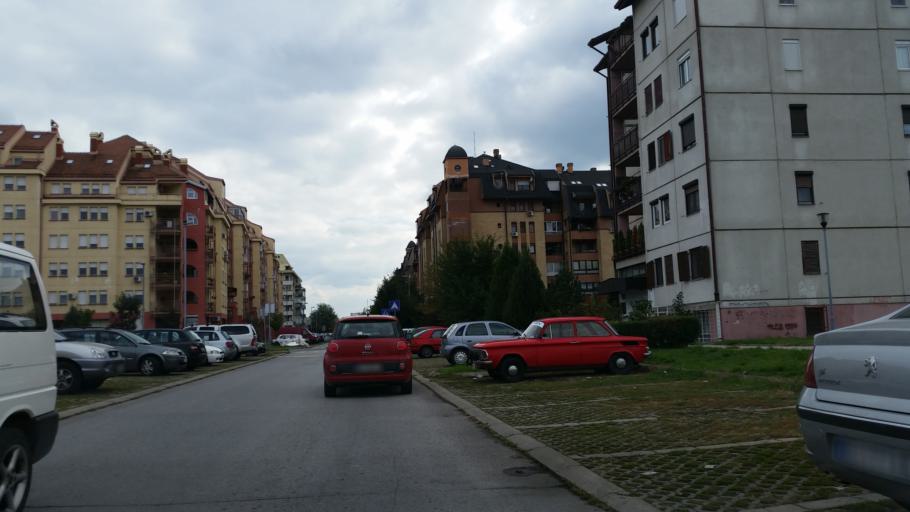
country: RS
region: Central Serbia
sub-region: Belgrade
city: Zemun
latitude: 44.8101
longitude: 20.3634
